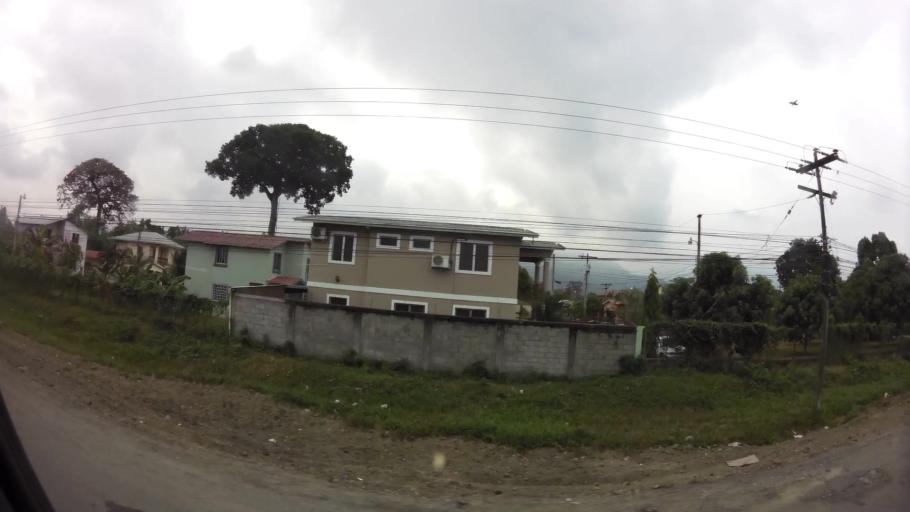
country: HN
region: Yoro
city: El Progreso
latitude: 15.4471
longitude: -87.7896
